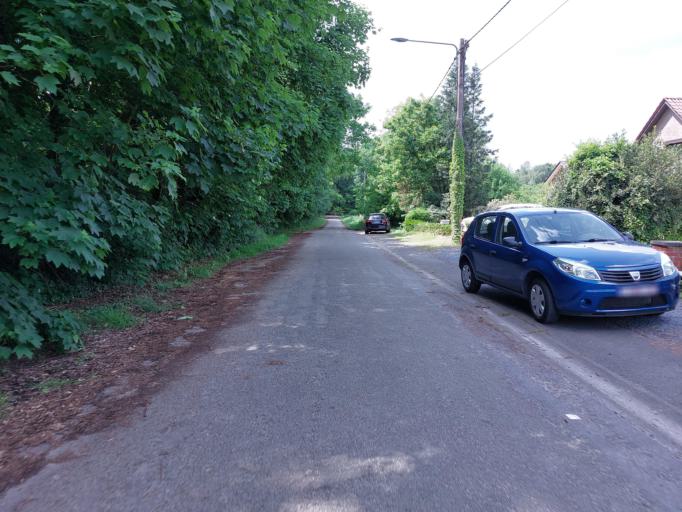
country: BE
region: Wallonia
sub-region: Province du Hainaut
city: Saint-Ghislain
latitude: 50.4815
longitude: 3.8199
